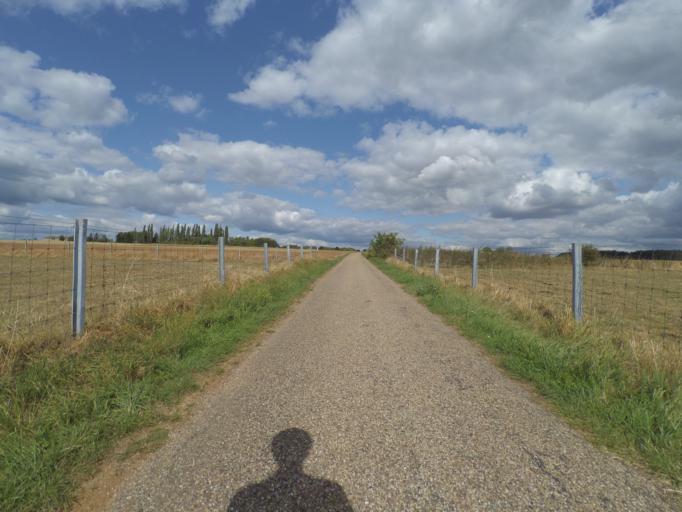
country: LU
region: Grevenmacher
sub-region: Canton de Remich
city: Dalheim
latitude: 49.5350
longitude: 6.2538
